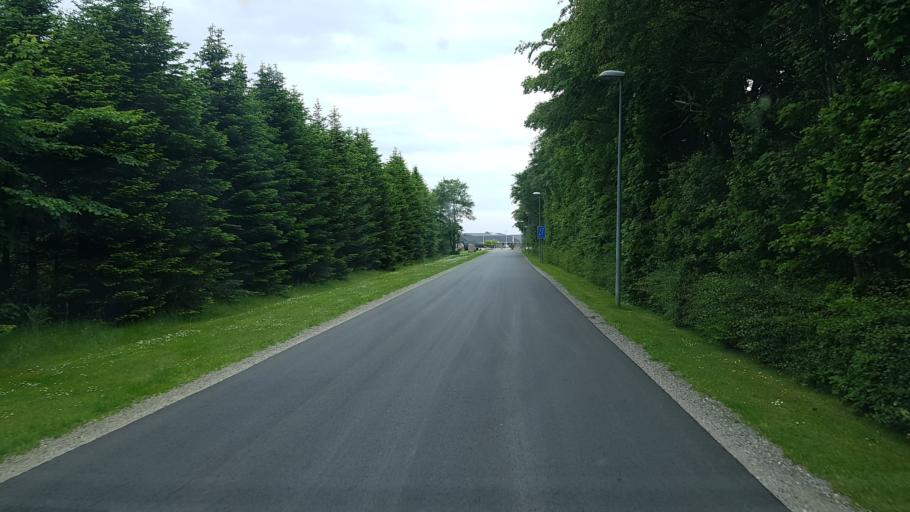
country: DK
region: South Denmark
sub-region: Varde Kommune
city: Oksbol
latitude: 55.7521
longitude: 8.3695
